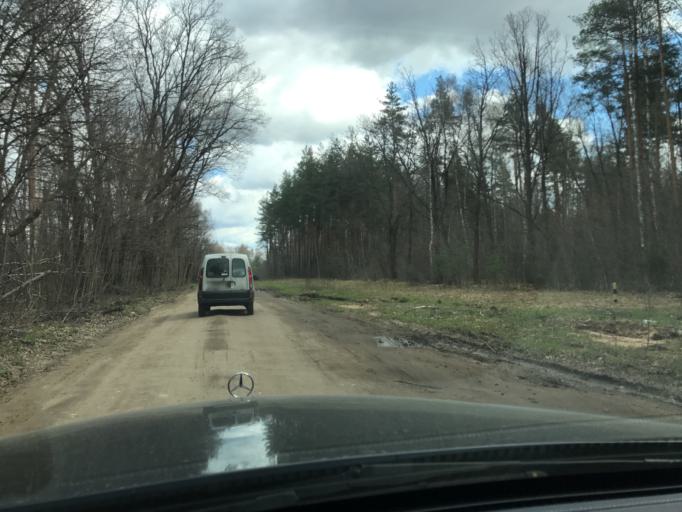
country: RU
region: Vladimir
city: Pokrov
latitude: 55.8768
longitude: 39.2460
